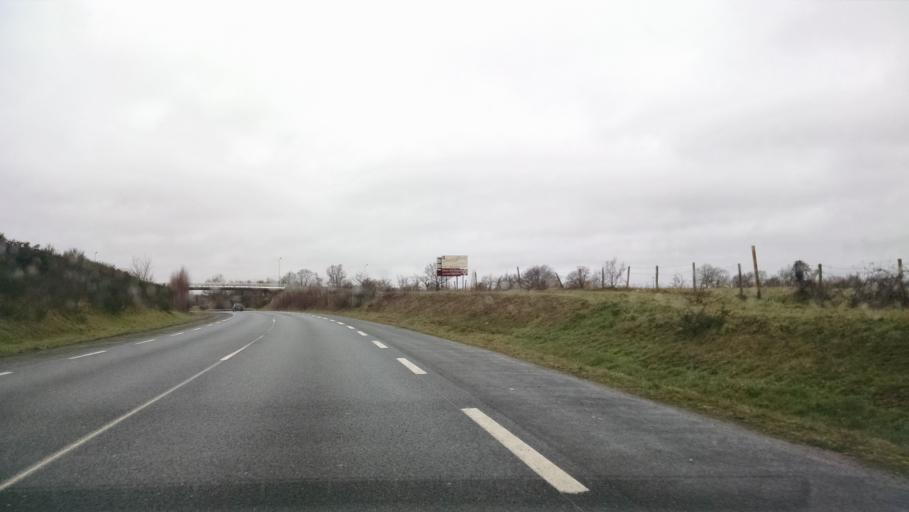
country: FR
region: Pays de la Loire
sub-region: Departement de la Loire-Atlantique
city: Clisson
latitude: 47.0982
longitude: -1.2741
